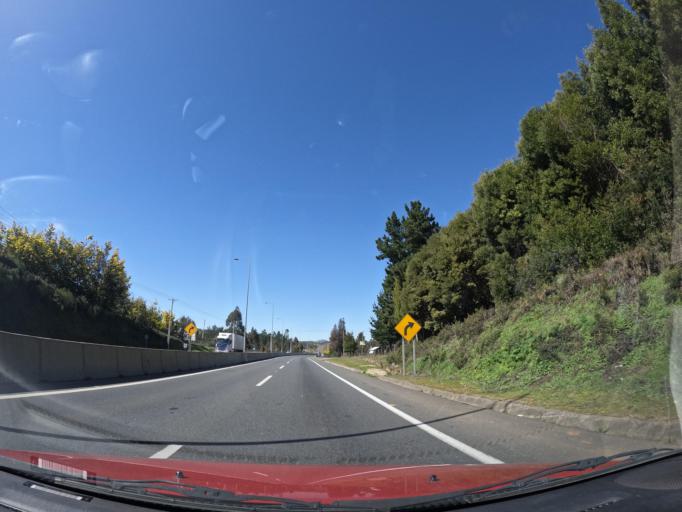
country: CL
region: Biobio
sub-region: Provincia de Concepcion
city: Chiguayante
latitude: -36.9050
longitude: -72.7834
